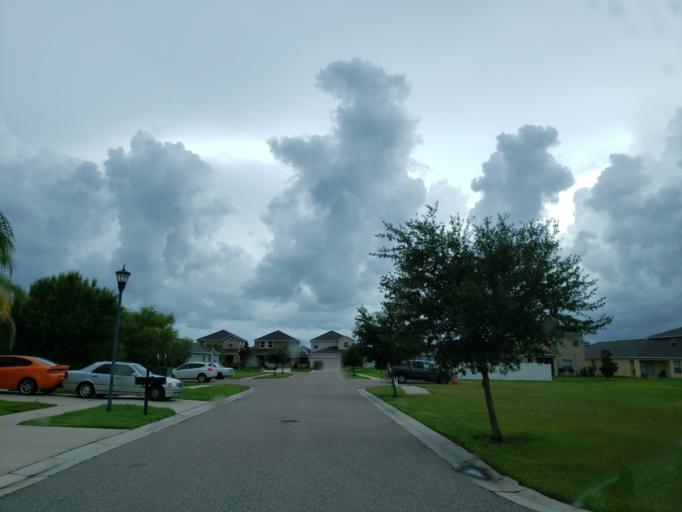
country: US
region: Florida
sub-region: Hillsborough County
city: Ruskin
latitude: 27.7303
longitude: -82.4059
